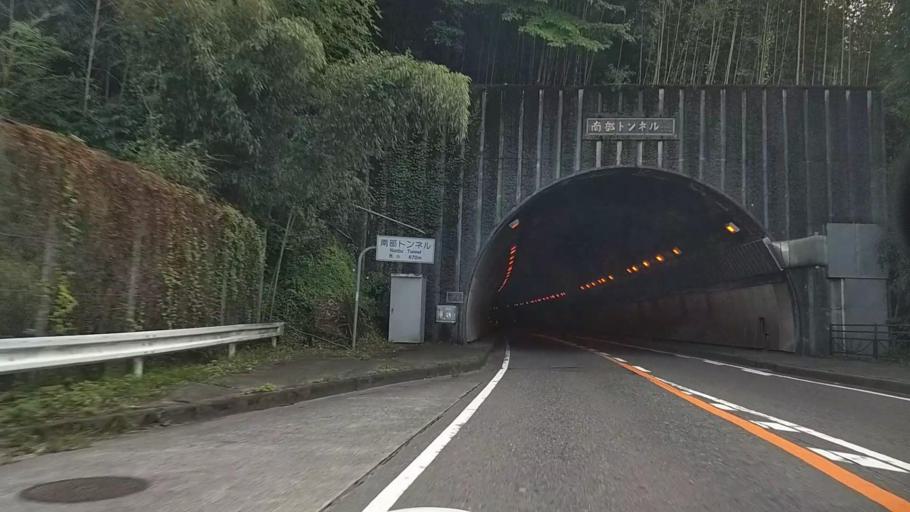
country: JP
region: Shizuoka
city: Fujinomiya
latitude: 35.2945
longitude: 138.4472
